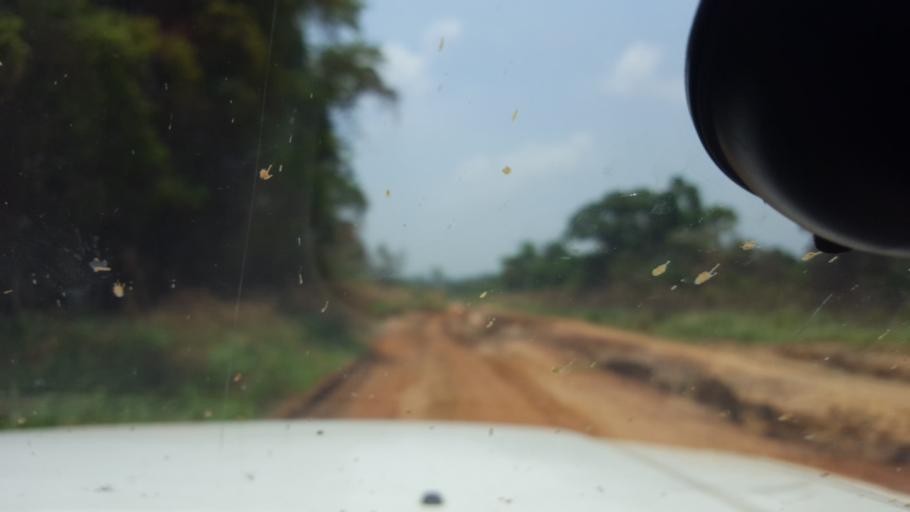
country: CD
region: Bandundu
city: Mushie
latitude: -3.7499
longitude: 16.6327
